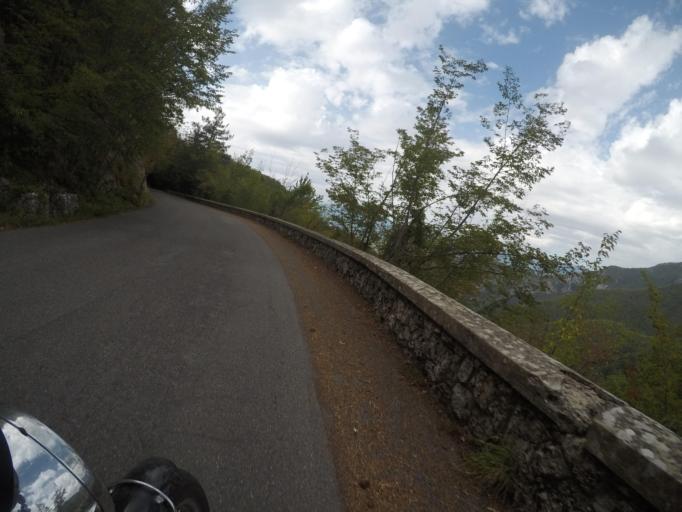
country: IT
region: Tuscany
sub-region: Provincia di Massa-Carrara
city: Carrara
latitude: 44.1244
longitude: 10.0978
